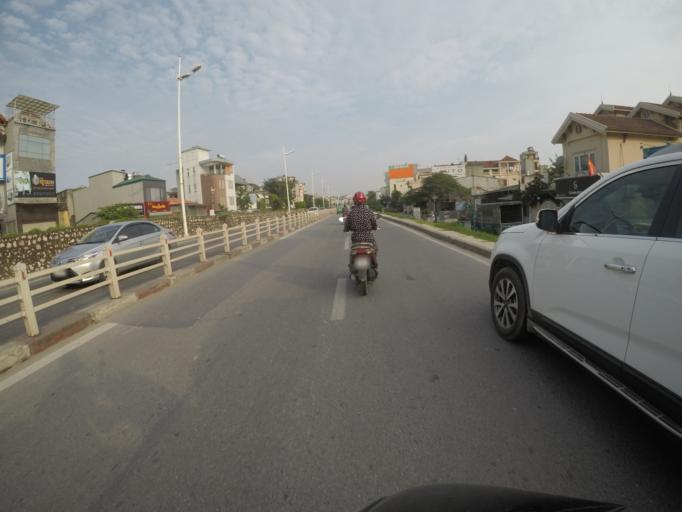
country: VN
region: Ha Noi
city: Tay Ho
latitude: 21.0754
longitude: 105.8226
